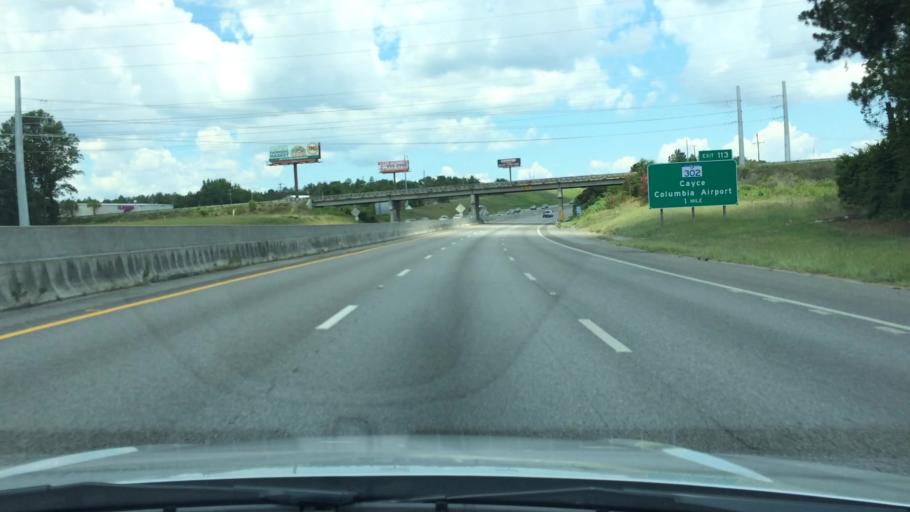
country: US
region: South Carolina
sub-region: Lexington County
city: Cayce
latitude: 33.9376
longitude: -81.0850
